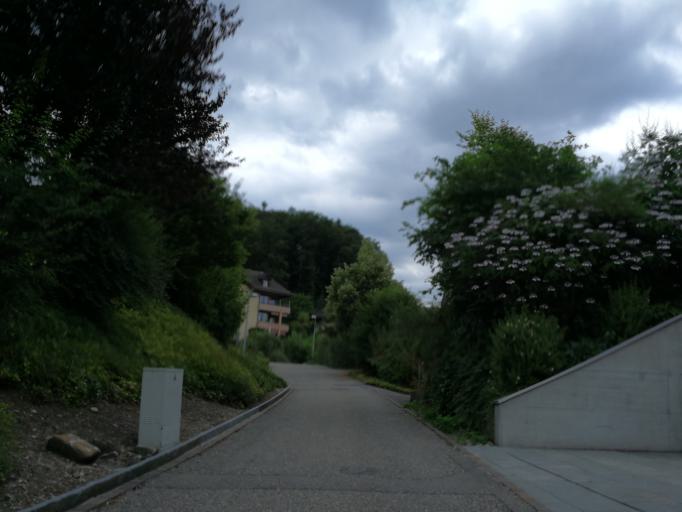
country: CH
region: Saint Gallen
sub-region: Wahlkreis See-Gaster
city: Jona
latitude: 47.2320
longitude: 8.8488
